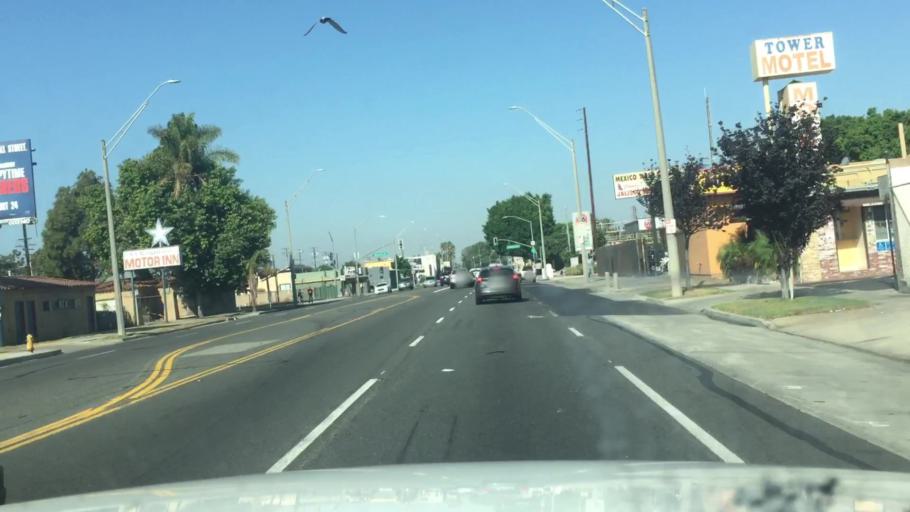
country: US
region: California
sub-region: Los Angeles County
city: Long Beach
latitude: 33.7899
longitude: -118.1967
